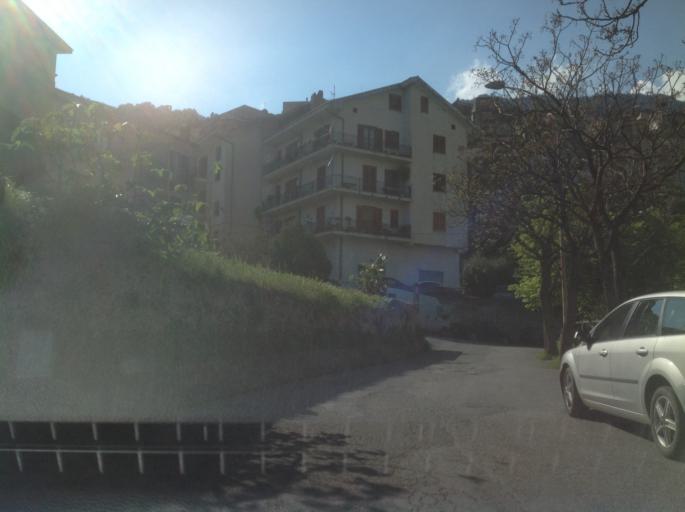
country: IT
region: Calabria
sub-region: Provincia di Cosenza
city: Civita
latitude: 39.8290
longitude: 16.3134
